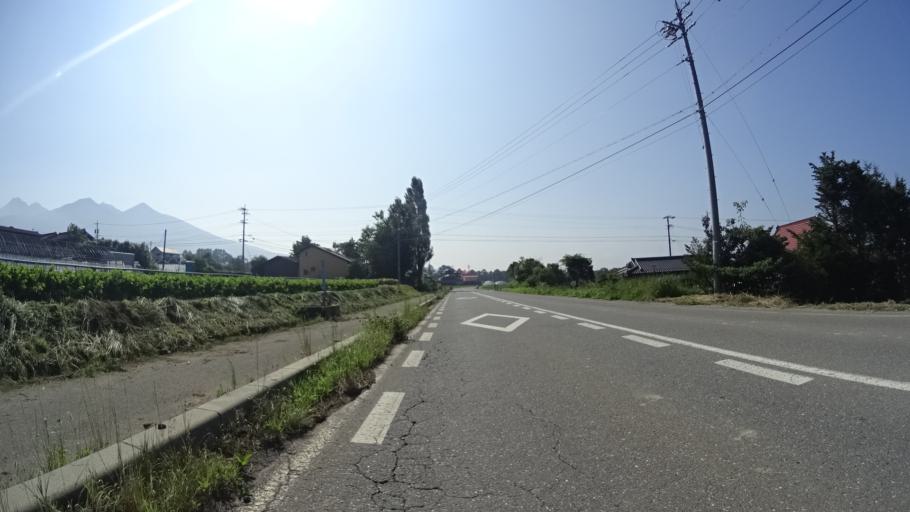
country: JP
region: Nagano
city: Chino
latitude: 35.9365
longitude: 138.2596
